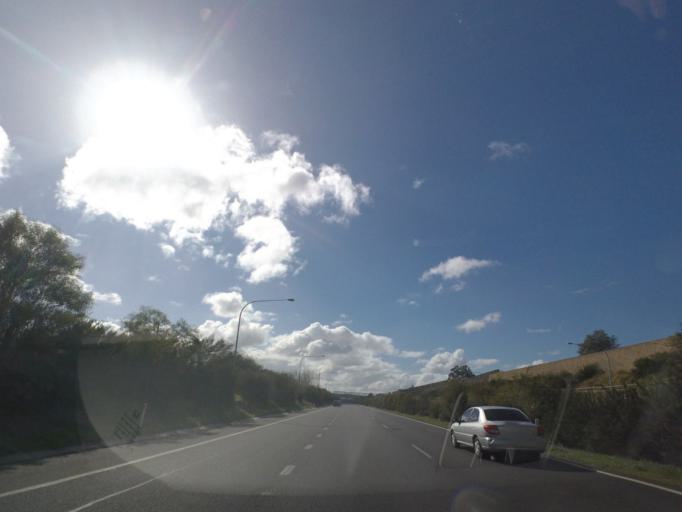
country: AU
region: New South Wales
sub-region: Albury Municipality
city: East Albury
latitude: -36.0864
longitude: 146.9251
